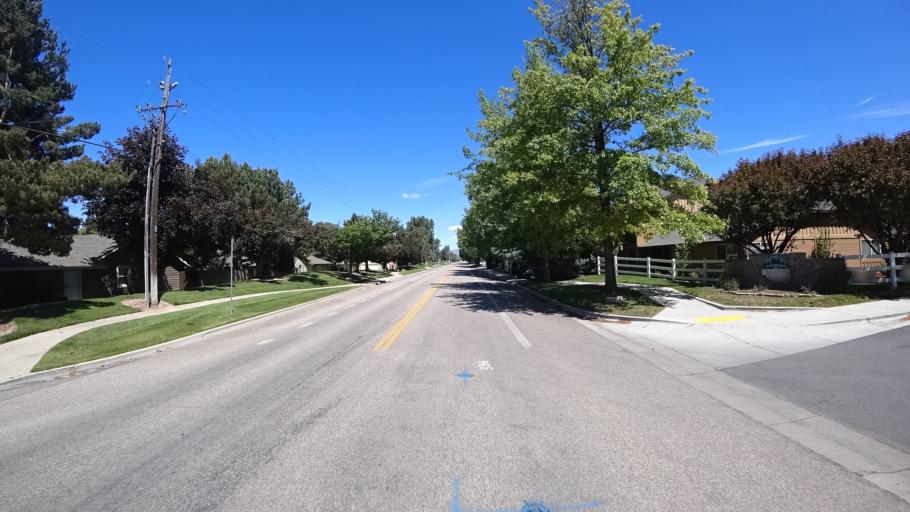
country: US
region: Idaho
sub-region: Ada County
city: Boise
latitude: 43.5718
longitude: -116.1835
